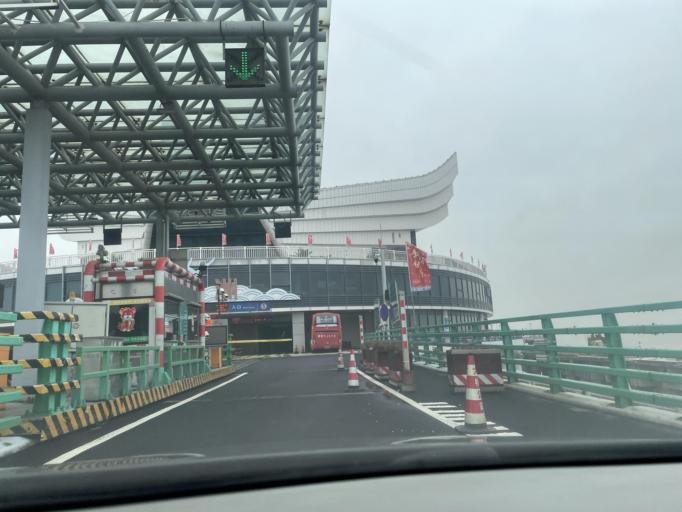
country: CN
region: Zhejiang Sheng
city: Zhapu
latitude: 30.4624
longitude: 121.1241
